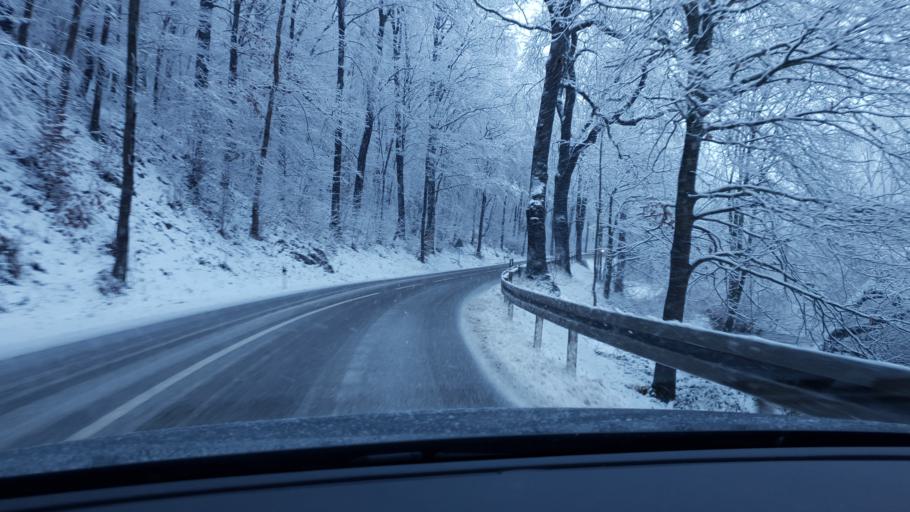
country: DE
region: Saxony
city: Taura
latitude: 50.9173
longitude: 12.8637
